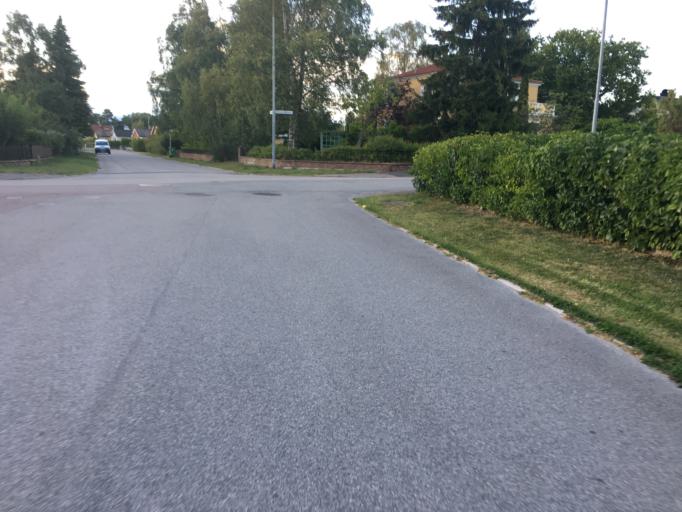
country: SE
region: Kalmar
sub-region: Kalmar Kommun
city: Kalmar
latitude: 56.6954
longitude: 16.3546
